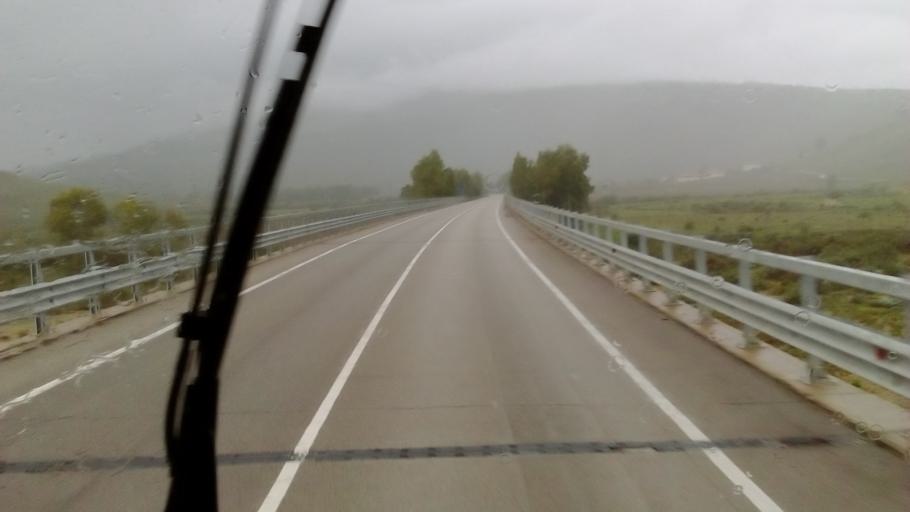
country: IT
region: Sicily
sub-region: Enna
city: Villarosa
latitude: 37.5315
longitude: 14.1297
